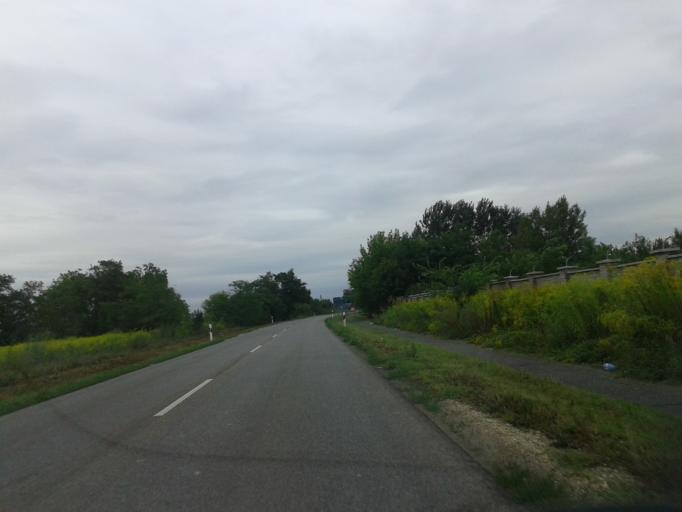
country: HU
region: Pest
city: Halasztelek
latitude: 47.3466
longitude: 18.9922
